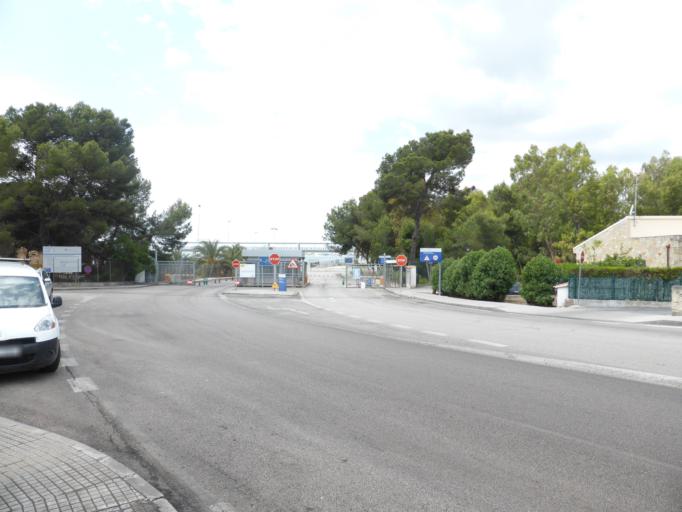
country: ES
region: Balearic Islands
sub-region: Illes Balears
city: Port d'Alcudia
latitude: 39.8368
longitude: 3.1425
